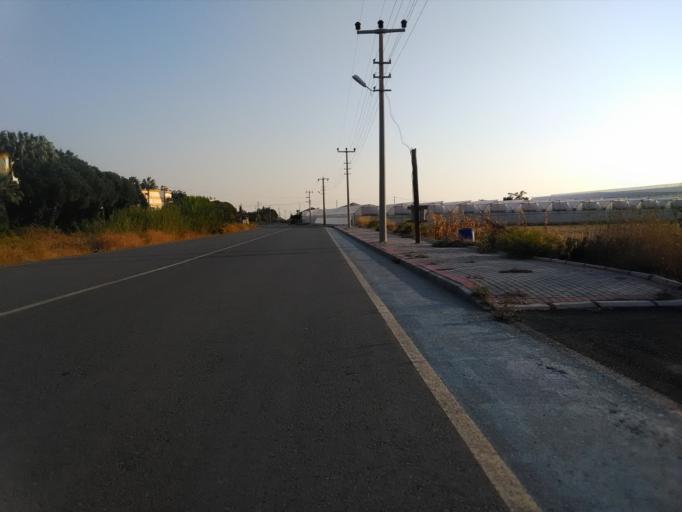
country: TR
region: Antalya
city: Gazipasa
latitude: 36.2576
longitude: 32.2906
